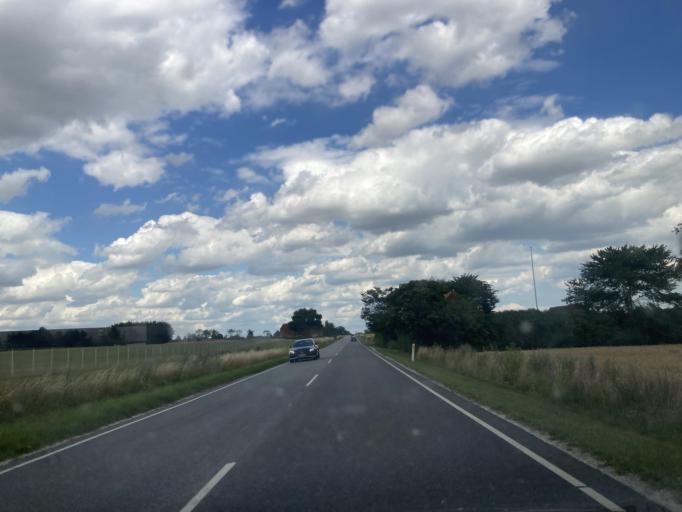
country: DK
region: Zealand
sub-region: Faxe Kommune
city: Haslev
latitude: 55.3340
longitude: 12.0234
